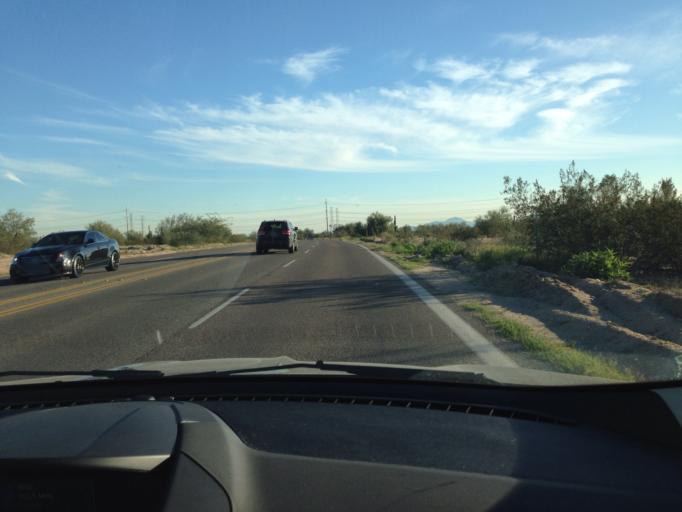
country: US
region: Arizona
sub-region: Maricopa County
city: Cave Creek
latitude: 33.7167
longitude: -111.9769
